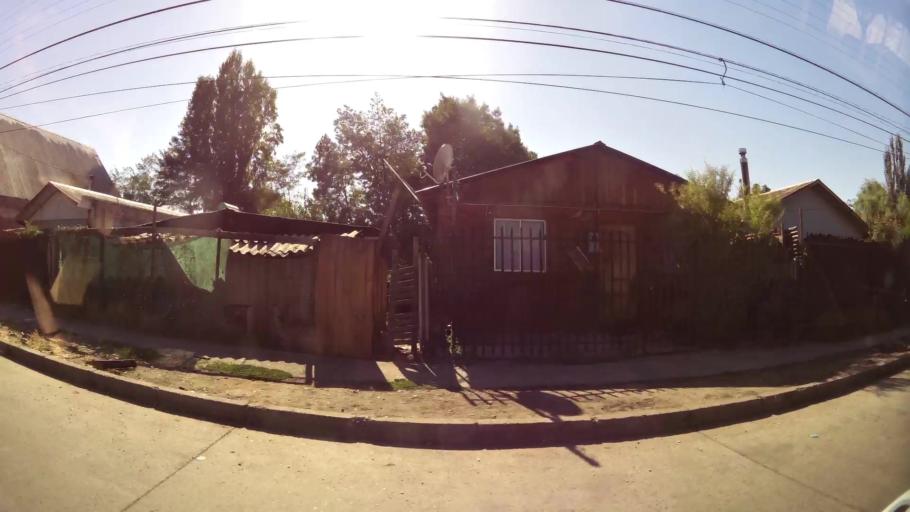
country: CL
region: Maule
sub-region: Provincia de Curico
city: Curico
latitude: -34.9985
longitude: -71.2458
